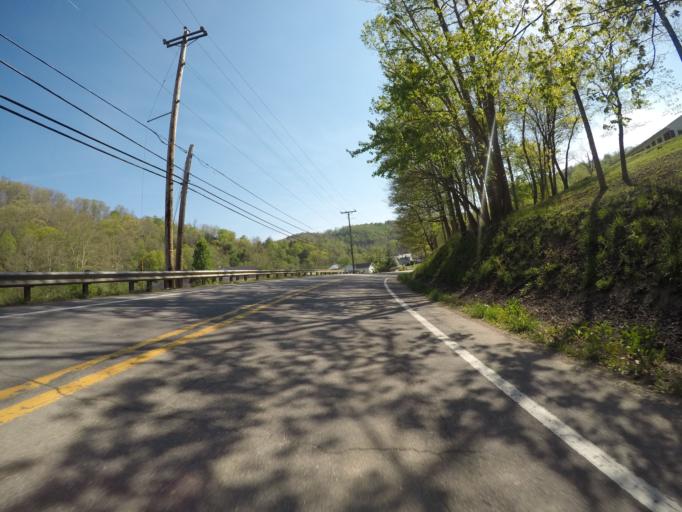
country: US
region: West Virginia
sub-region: Kanawha County
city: Clendenin
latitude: 38.5124
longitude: -81.3566
